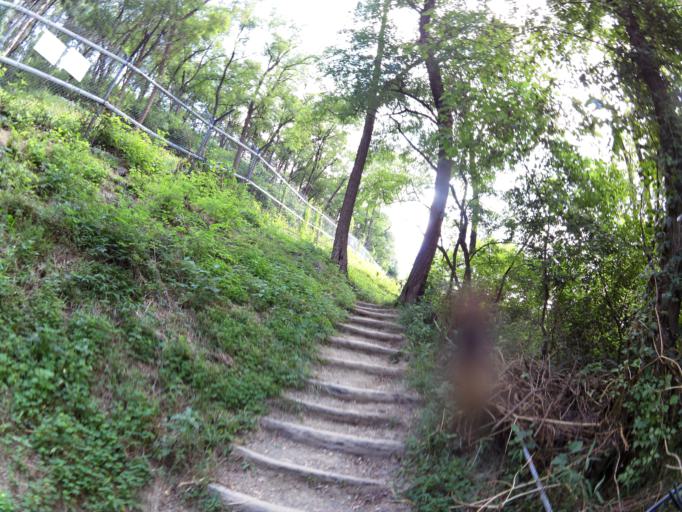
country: KR
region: Daegu
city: Daegu
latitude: 35.8608
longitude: 128.6551
